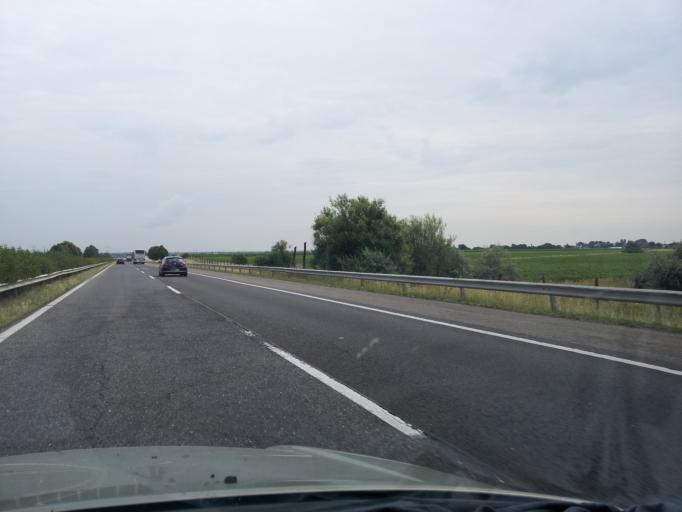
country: HU
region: Heves
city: Hort
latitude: 47.6946
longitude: 19.7599
